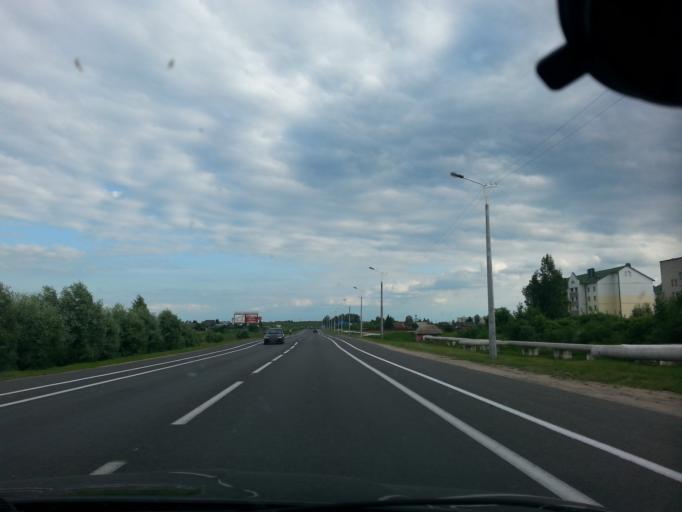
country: BY
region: Minsk
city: Myadzyel
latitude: 54.8824
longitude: 26.9389
